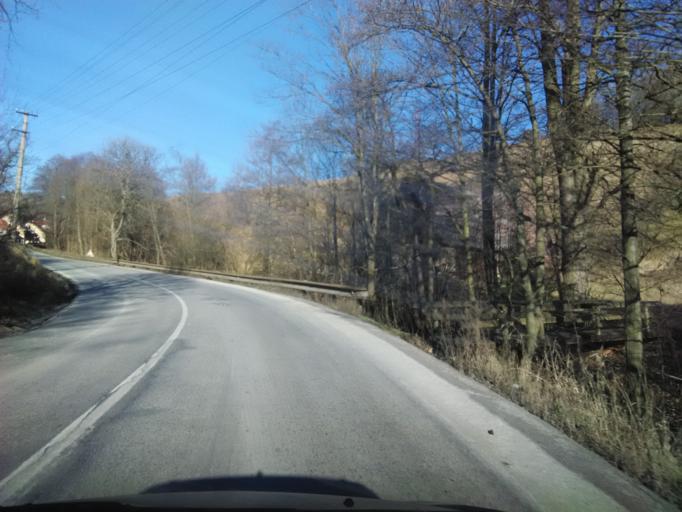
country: SK
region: Banskobystricky
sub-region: Okres Ziar nad Hronom
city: Kremnica
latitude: 48.7161
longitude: 18.9183
